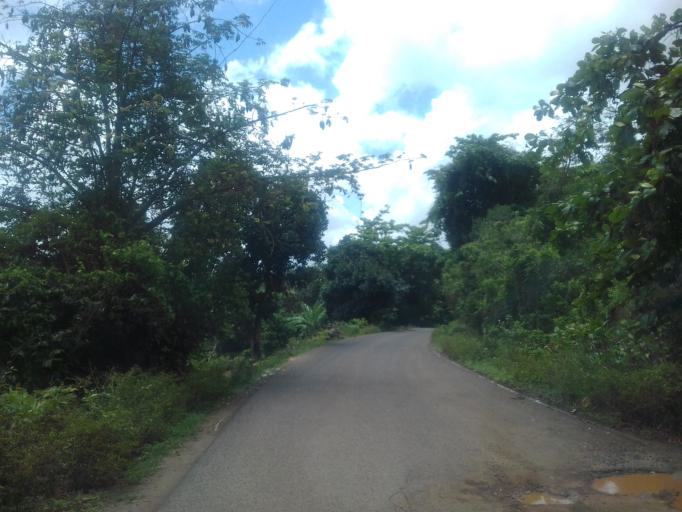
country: MG
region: Sava
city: Sambava
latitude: -14.1182
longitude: 50.0603
